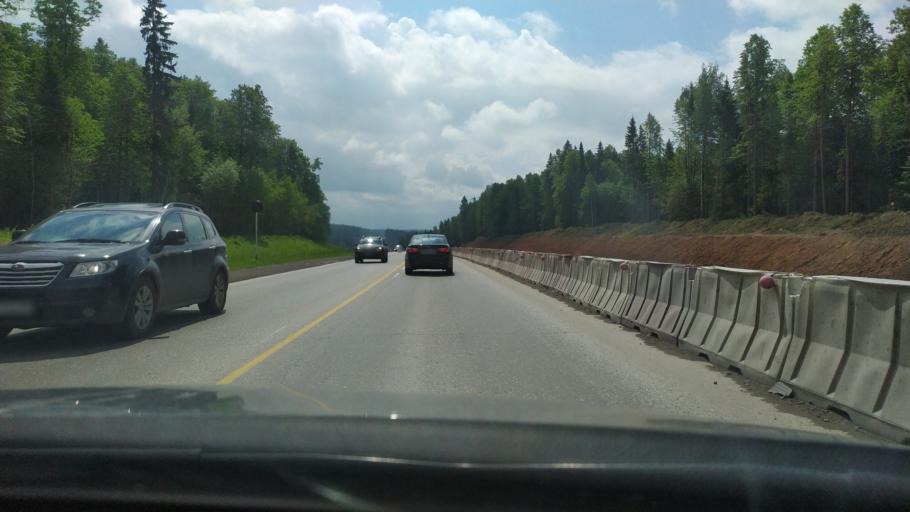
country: RU
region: Perm
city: Novyye Lyady
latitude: 58.0988
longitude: 56.4251
